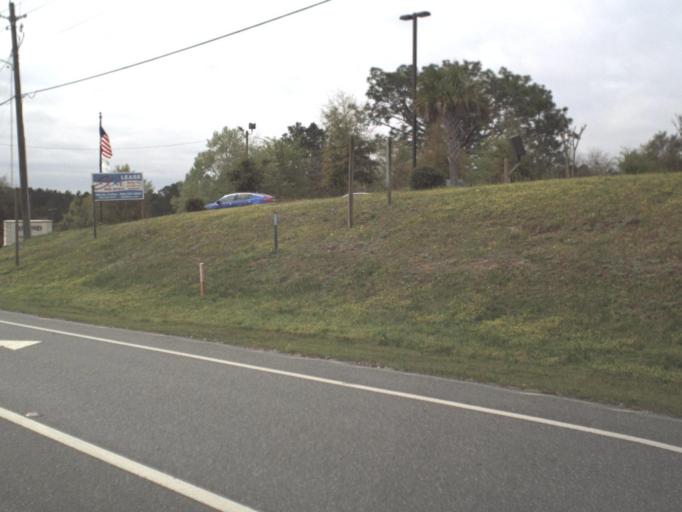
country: US
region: Florida
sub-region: Okaloosa County
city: Crestview
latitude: 30.7154
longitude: -86.5699
